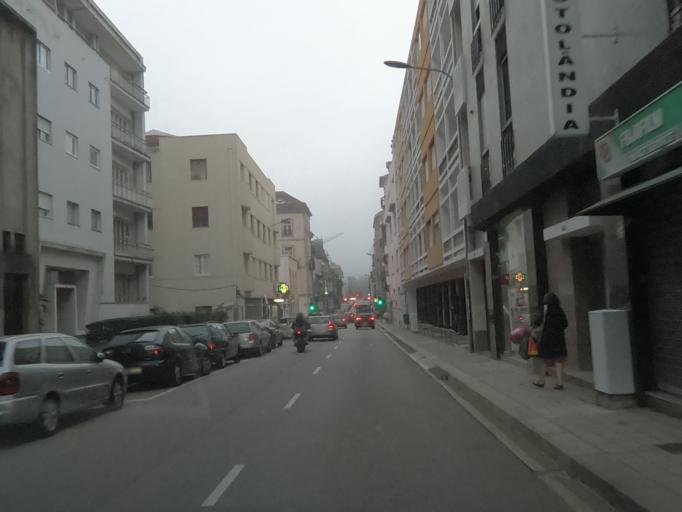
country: PT
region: Porto
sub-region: Porto
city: Porto
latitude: 41.1564
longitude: -8.6198
